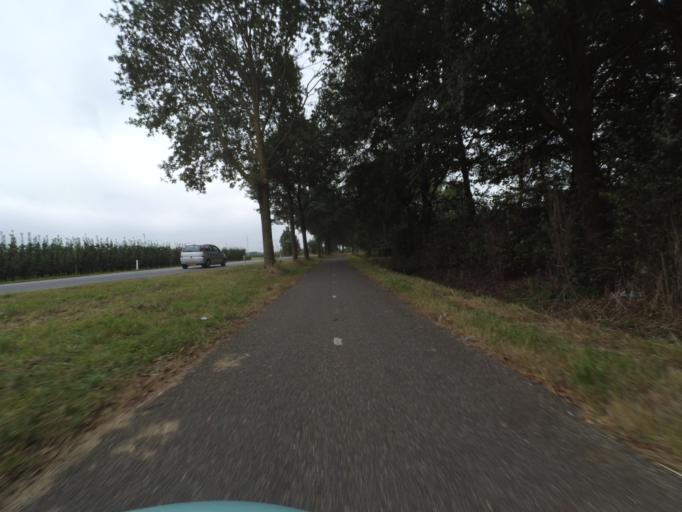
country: NL
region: Utrecht
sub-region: Gemeente Wijk bij Duurstede
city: Wijk bij Duurstede
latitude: 51.9257
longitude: 5.3239
